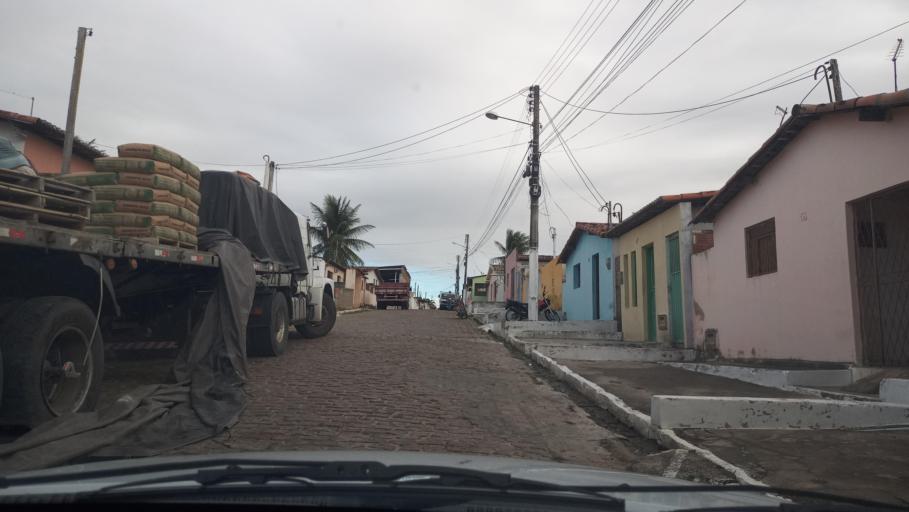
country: BR
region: Rio Grande do Norte
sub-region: Brejinho
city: Brejinho
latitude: -6.0443
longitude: -35.4325
